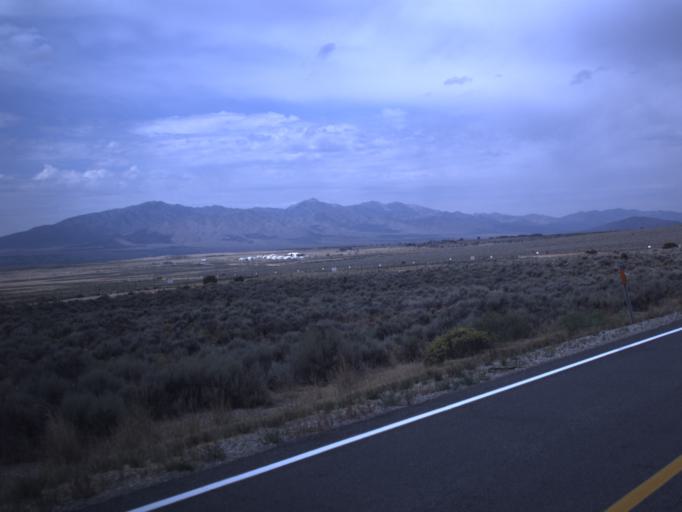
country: US
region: Utah
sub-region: Tooele County
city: Tooele
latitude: 40.3025
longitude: -112.2773
